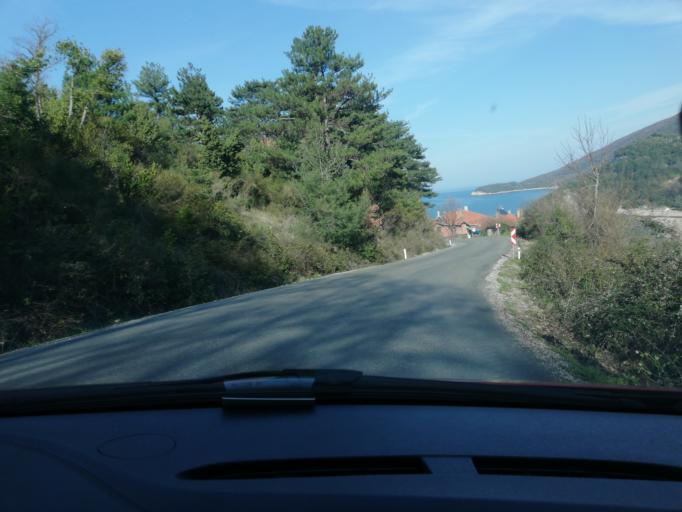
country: TR
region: Bartin
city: Kurucasile
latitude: 41.8464
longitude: 32.7492
